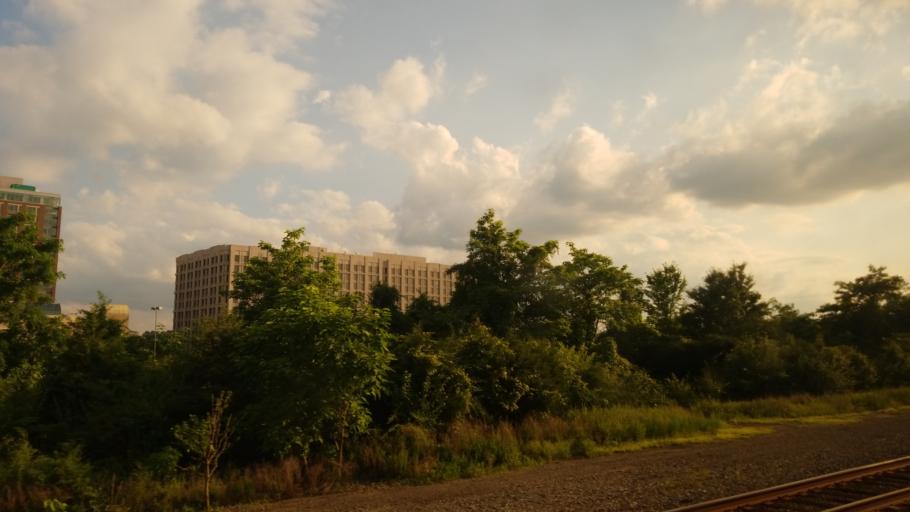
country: US
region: Virginia
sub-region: Fairfax County
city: Huntington
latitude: 38.8045
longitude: -77.0702
